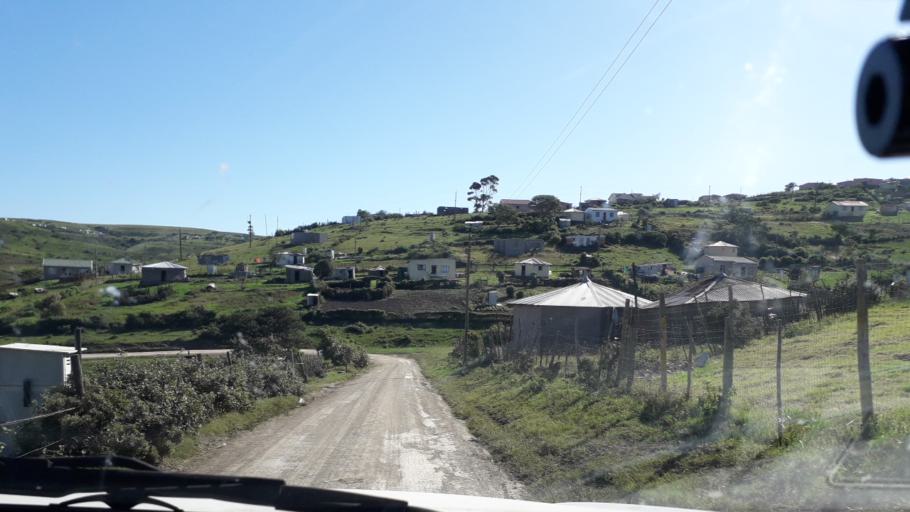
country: ZA
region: Eastern Cape
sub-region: Buffalo City Metropolitan Municipality
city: East London
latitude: -32.7982
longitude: 27.9703
